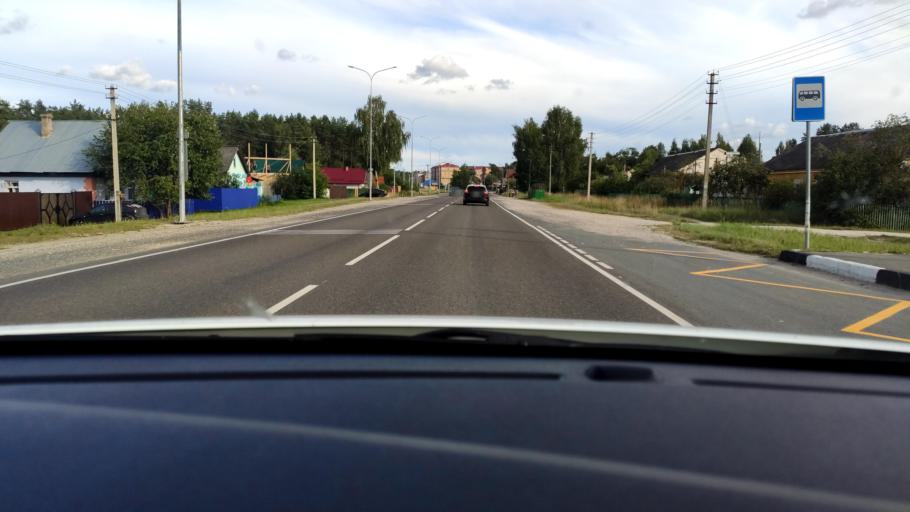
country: RU
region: Mariy-El
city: Suslonger
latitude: 56.3836
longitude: 48.1956
